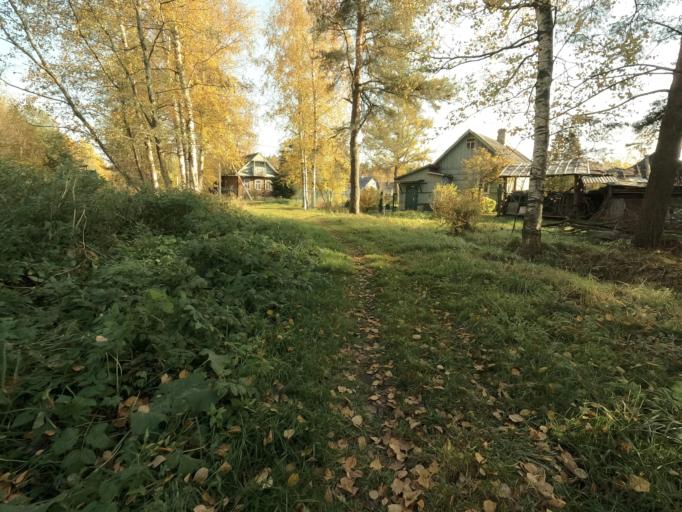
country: RU
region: Leningrad
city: Mga
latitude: 59.7476
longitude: 31.0723
